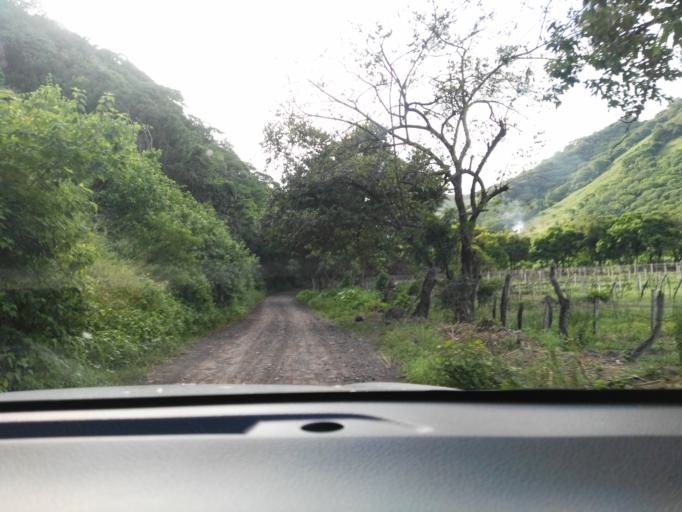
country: NI
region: Matagalpa
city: Terrabona
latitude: 12.8409
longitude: -86.0202
